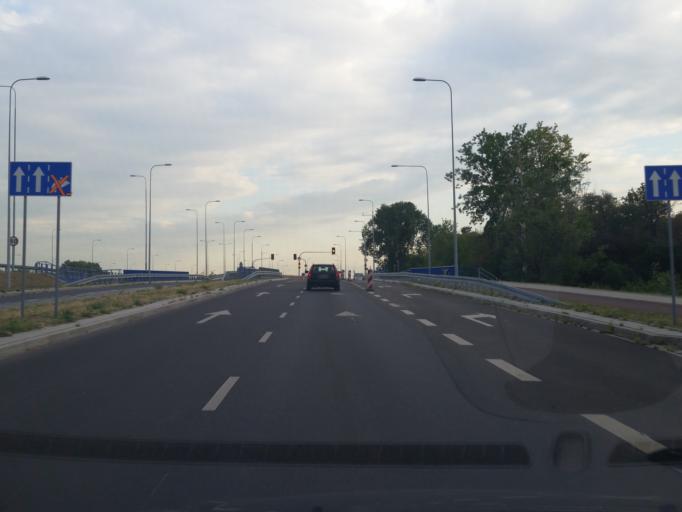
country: PL
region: Masovian Voivodeship
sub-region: Warszawa
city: Wlochy
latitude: 52.1720
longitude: 20.9853
